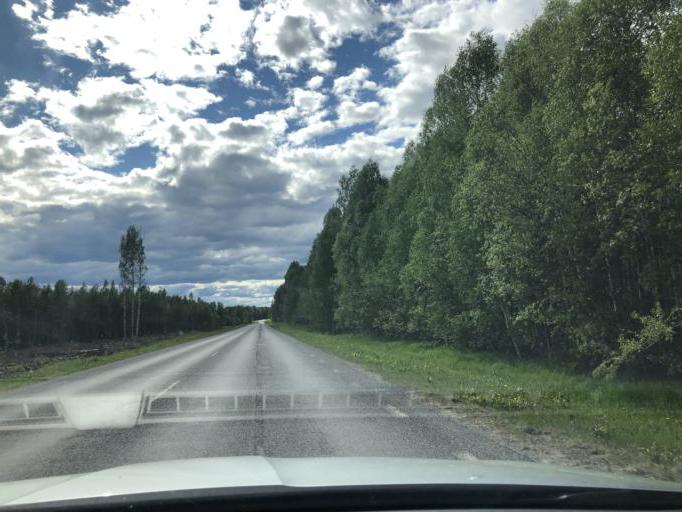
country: SE
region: Norrbotten
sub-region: Alvsbyns Kommun
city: AElvsbyn
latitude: 65.6945
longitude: 20.6314
